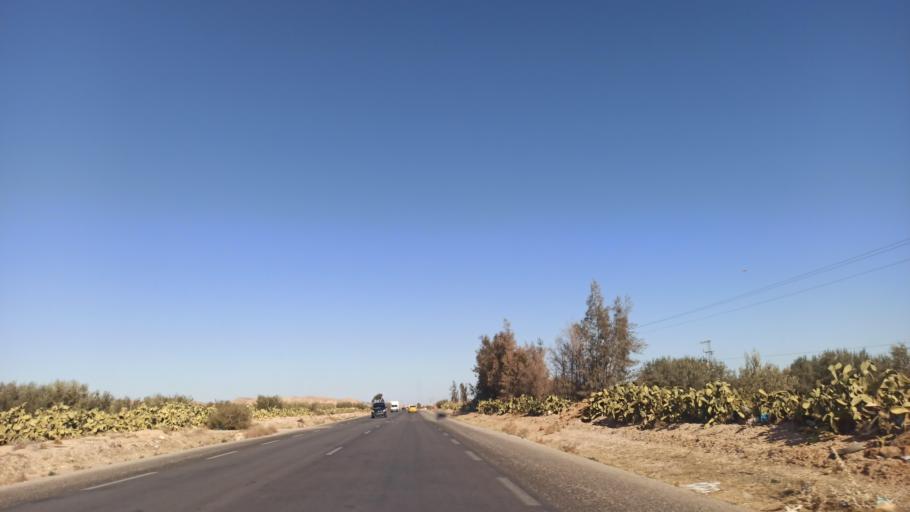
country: TN
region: Sidi Bu Zayd
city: Bi'r al Hufayy
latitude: 34.8978
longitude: 9.1732
